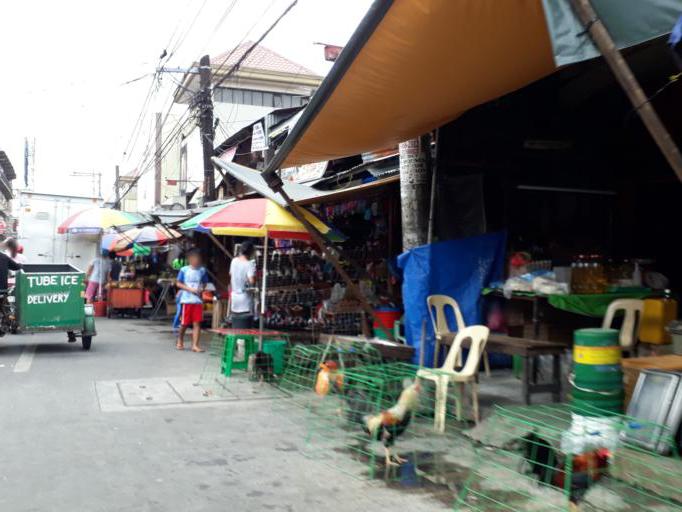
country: PH
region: Metro Manila
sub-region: City of Manila
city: Manila
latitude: 14.6095
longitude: 120.9962
